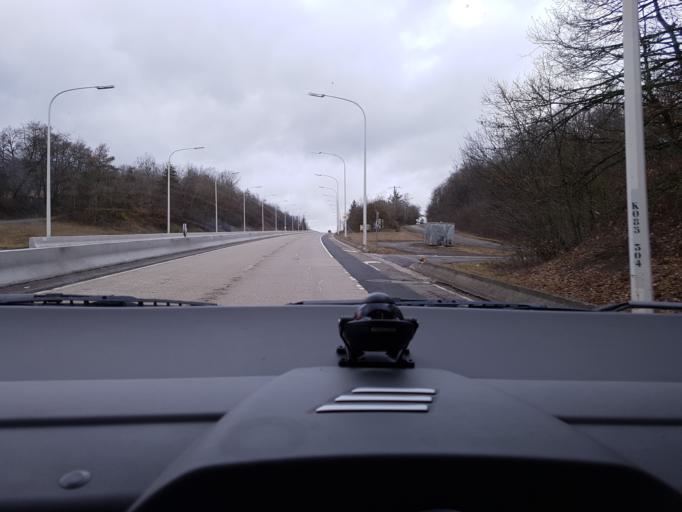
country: BE
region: Wallonia
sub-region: Province du Luxembourg
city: Marche-en-Famenne
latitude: 50.2562
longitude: 5.2682
